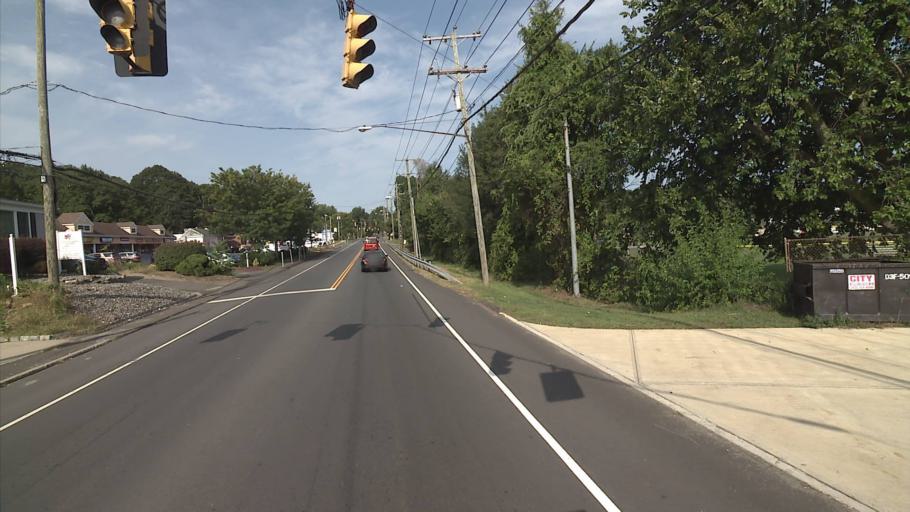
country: US
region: Connecticut
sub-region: Fairfield County
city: Norwalk
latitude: 41.1273
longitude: -73.4326
